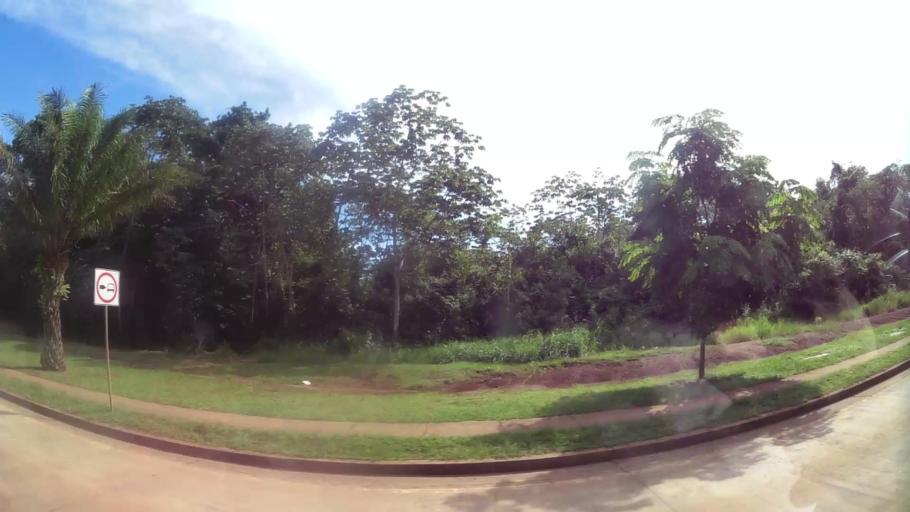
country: PA
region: Panama
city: Puerto Caimito
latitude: 8.8876
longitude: -79.7452
